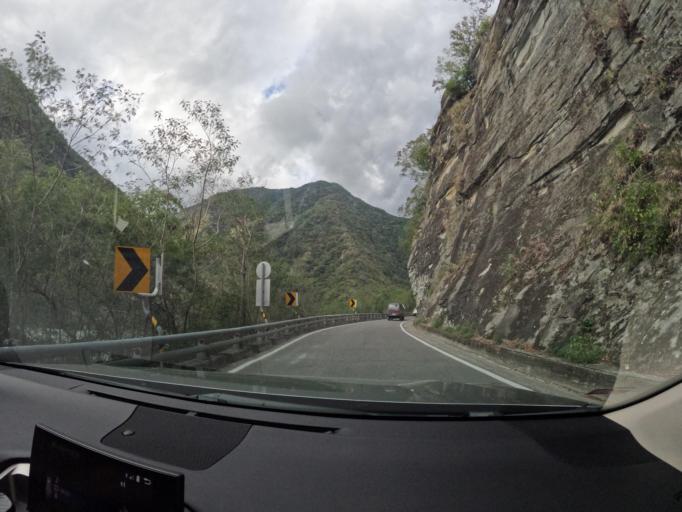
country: TW
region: Taiwan
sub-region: Taitung
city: Taitung
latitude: 23.1355
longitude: 121.1233
